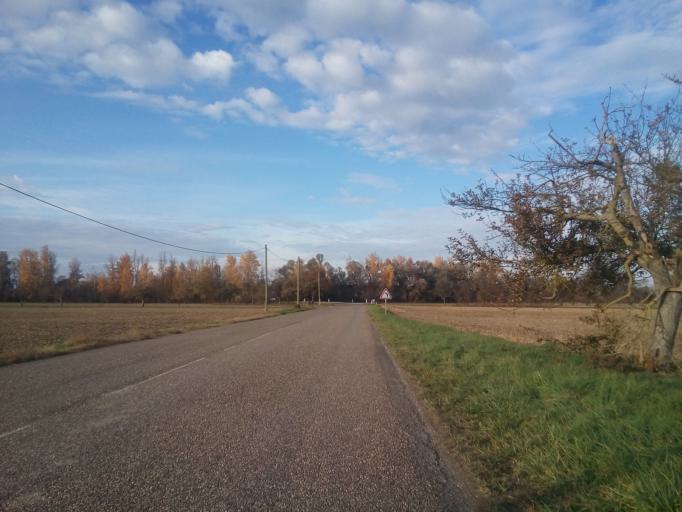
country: FR
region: Alsace
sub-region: Departement du Bas-Rhin
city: Herrlisheim
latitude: 48.7010
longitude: 7.9208
